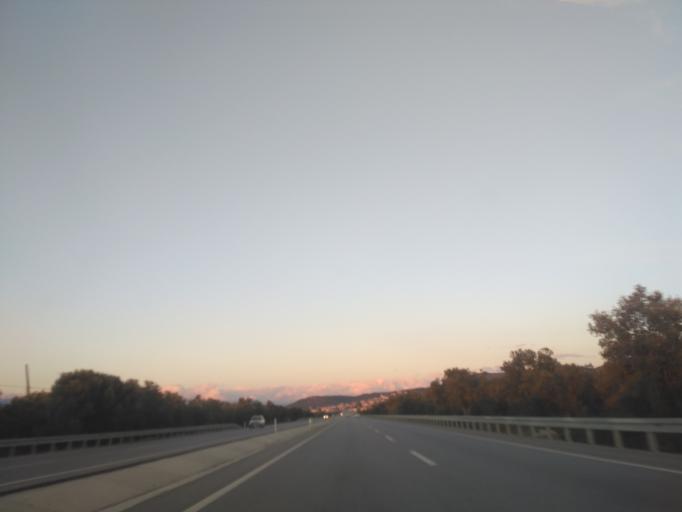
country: TR
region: Balikesir
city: Emrutabat
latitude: 39.4089
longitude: 26.8513
